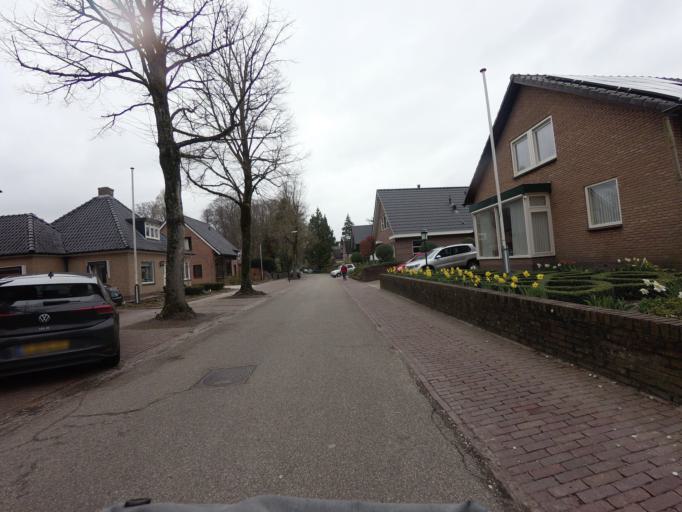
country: NL
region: Gelderland
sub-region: Gemeente Apeldoorn
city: Apeldoorn
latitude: 52.2345
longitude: 5.9506
